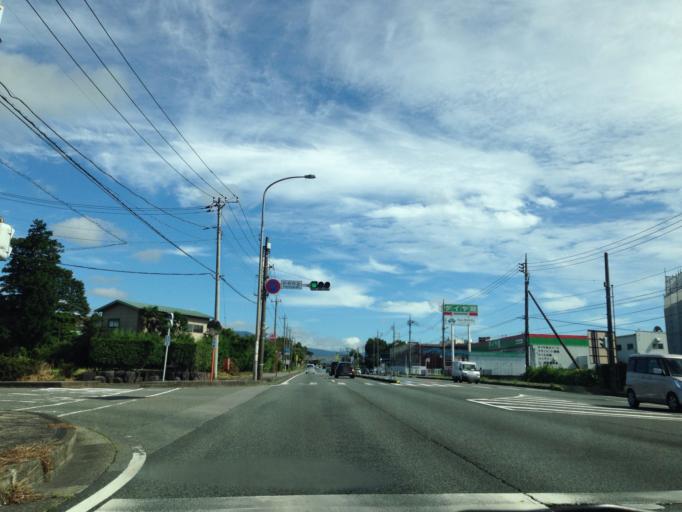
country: JP
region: Shizuoka
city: Gotemba
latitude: 35.2921
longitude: 138.9197
